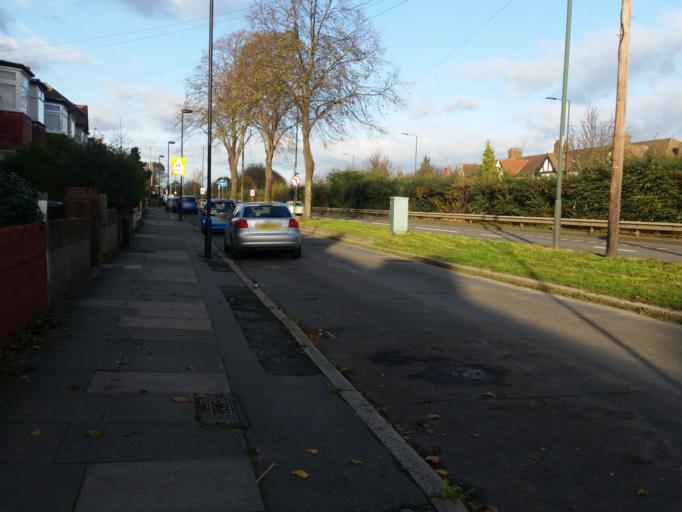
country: GB
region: England
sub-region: Greater London
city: Enfield
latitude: 51.6232
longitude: -0.0822
